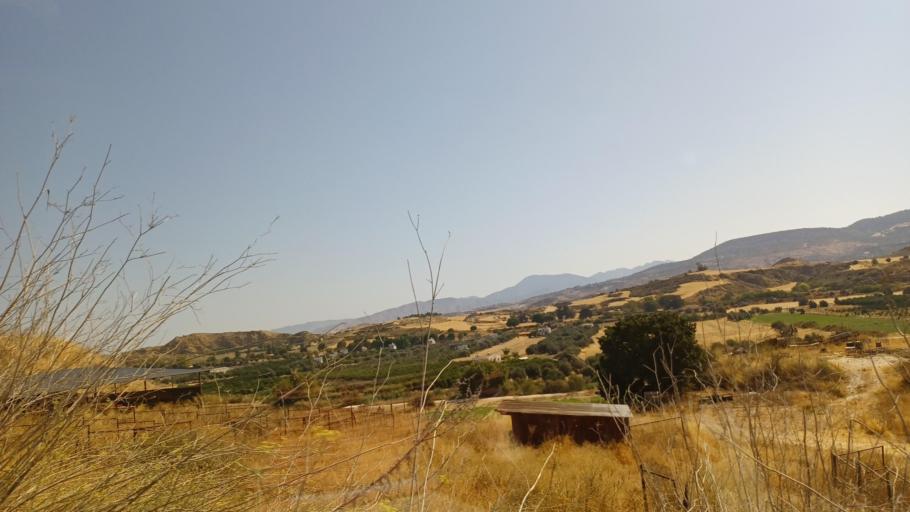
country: CY
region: Pafos
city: Polis
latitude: 35.0111
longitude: 32.4276
